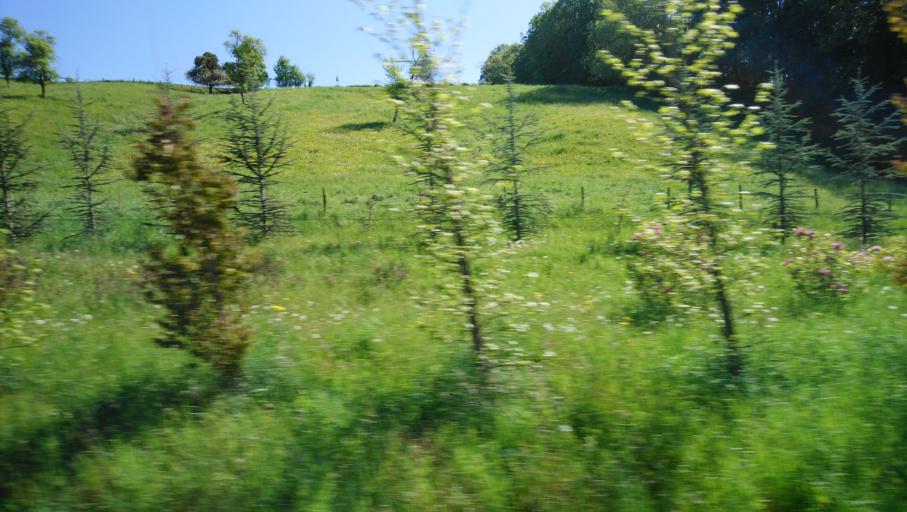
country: LU
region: Diekirch
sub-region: Canton de Vianden
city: Tandel
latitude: 49.8766
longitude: 6.1893
